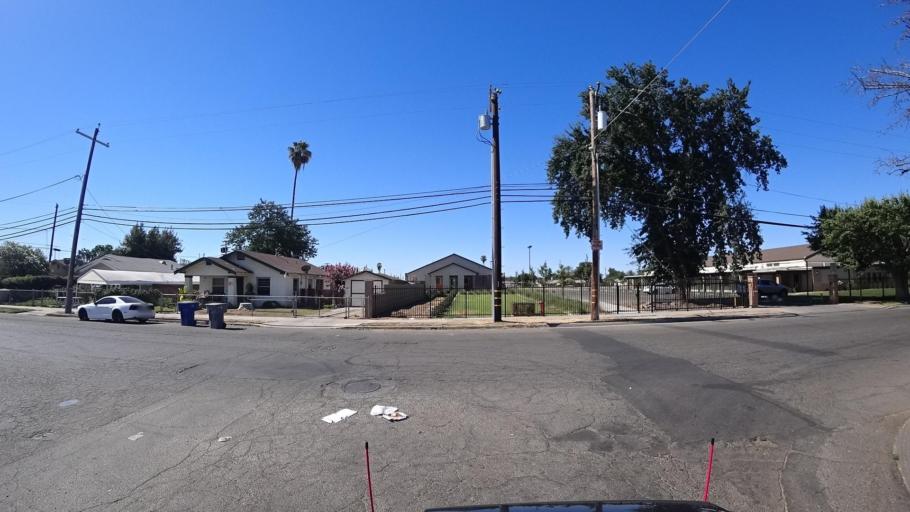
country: US
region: California
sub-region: Fresno County
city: Fresno
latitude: 36.7179
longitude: -119.7920
